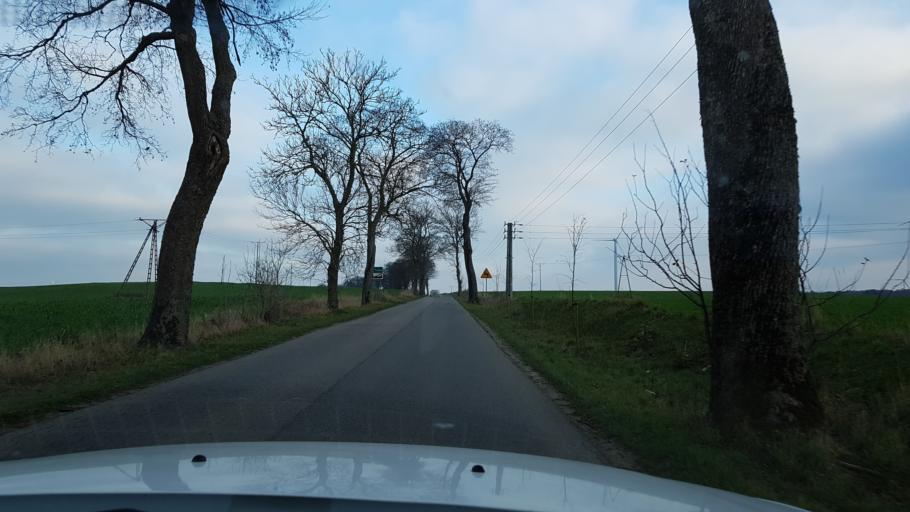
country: PL
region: West Pomeranian Voivodeship
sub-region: Powiat kolobrzeski
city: Goscino
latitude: 54.0541
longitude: 15.6877
